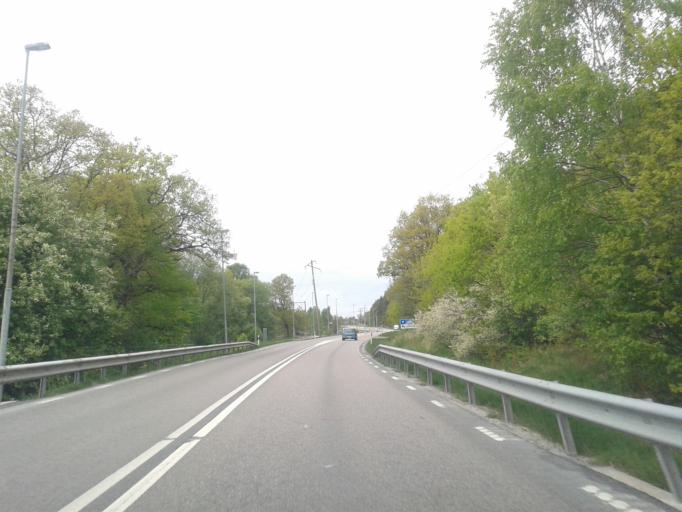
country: SE
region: Vaestra Goetaland
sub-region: Kungalvs Kommun
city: Kungalv
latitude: 57.8680
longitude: 11.9150
